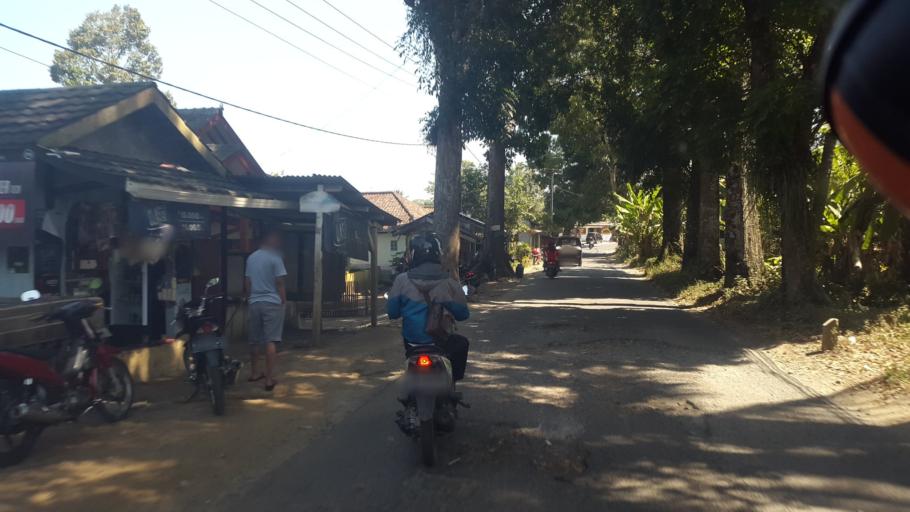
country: ID
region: West Java
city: Cicurug
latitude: -6.8350
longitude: 106.6684
